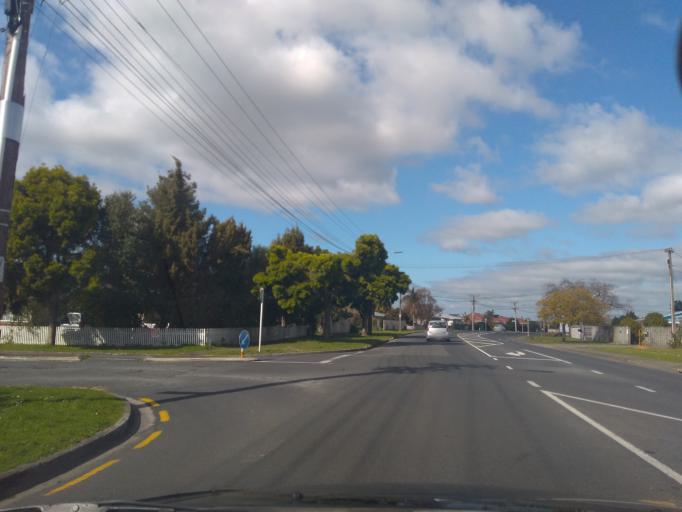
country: NZ
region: Northland
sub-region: Whangarei
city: Whangarei
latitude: -35.6910
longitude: 174.3272
